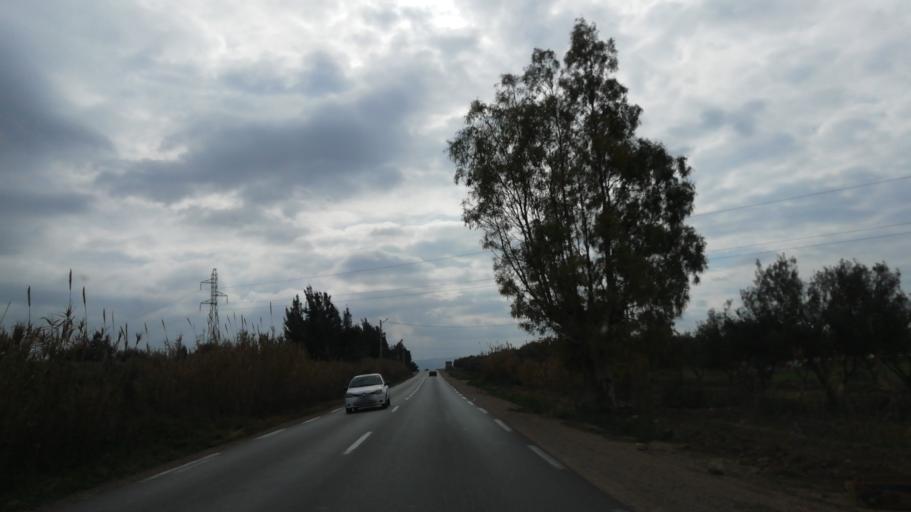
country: DZ
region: Oran
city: Sidi ech Chahmi
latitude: 35.5736
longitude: -0.4510
